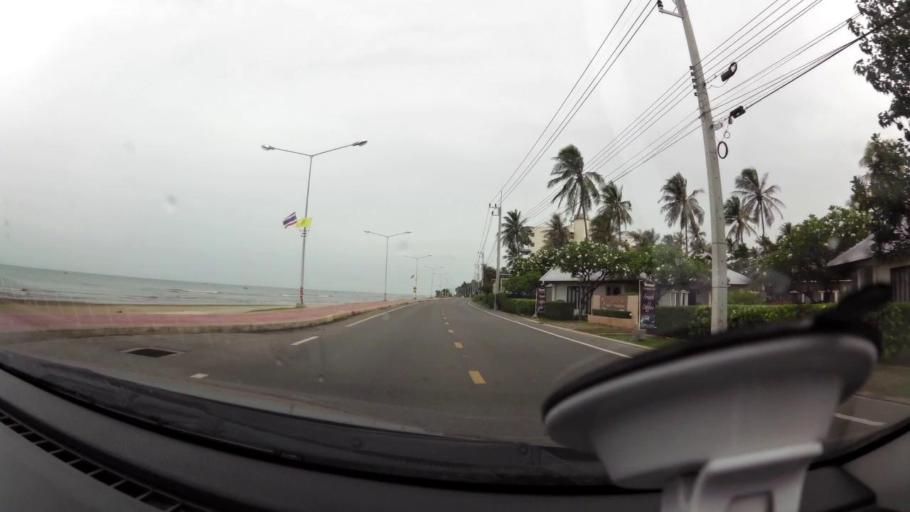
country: TH
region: Prachuap Khiri Khan
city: Pran Buri
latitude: 12.3930
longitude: 99.9966
